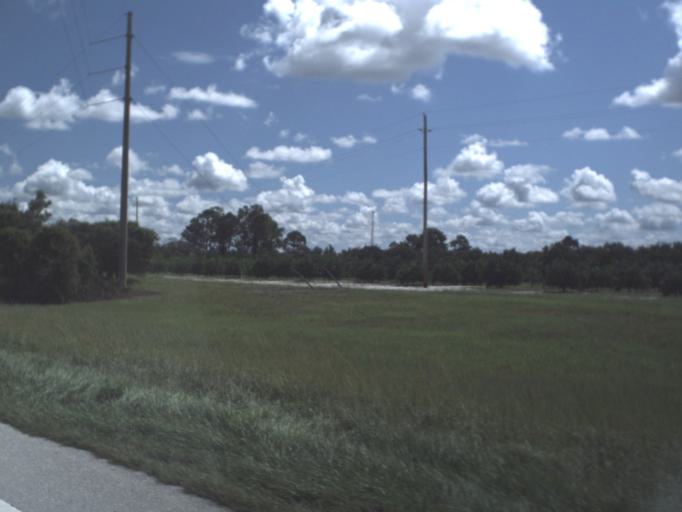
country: US
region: Florida
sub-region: Highlands County
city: Placid Lakes
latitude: 27.2088
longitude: -81.3593
